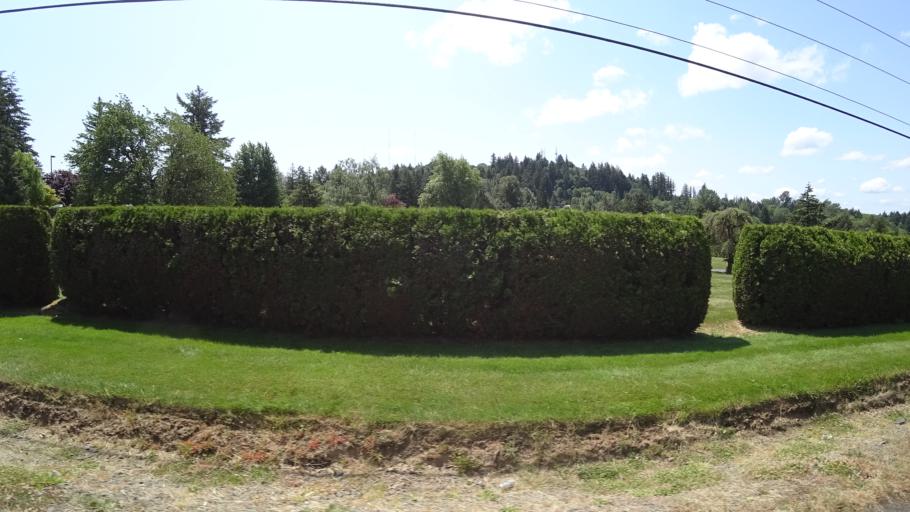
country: US
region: Oregon
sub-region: Clackamas County
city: Happy Valley
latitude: 45.4603
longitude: -122.5449
